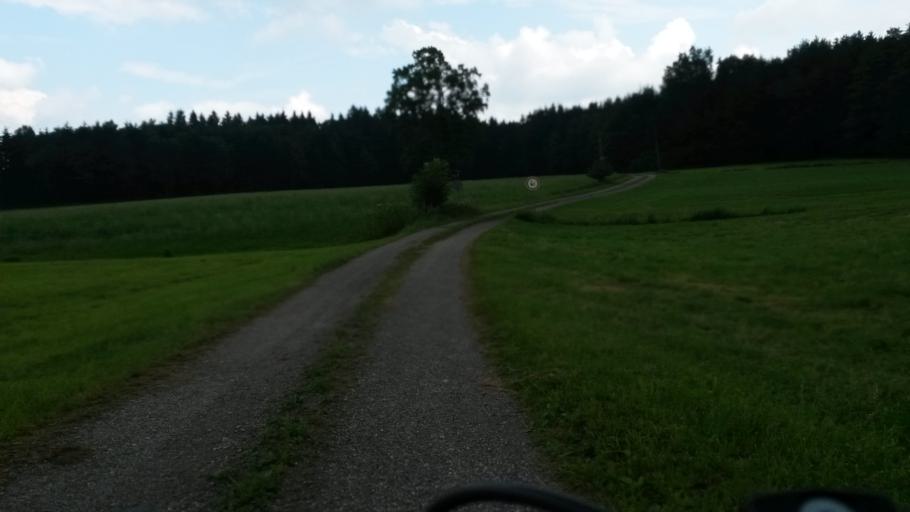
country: DE
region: Bavaria
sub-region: Upper Bavaria
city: Amerang
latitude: 47.9700
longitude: 12.3062
